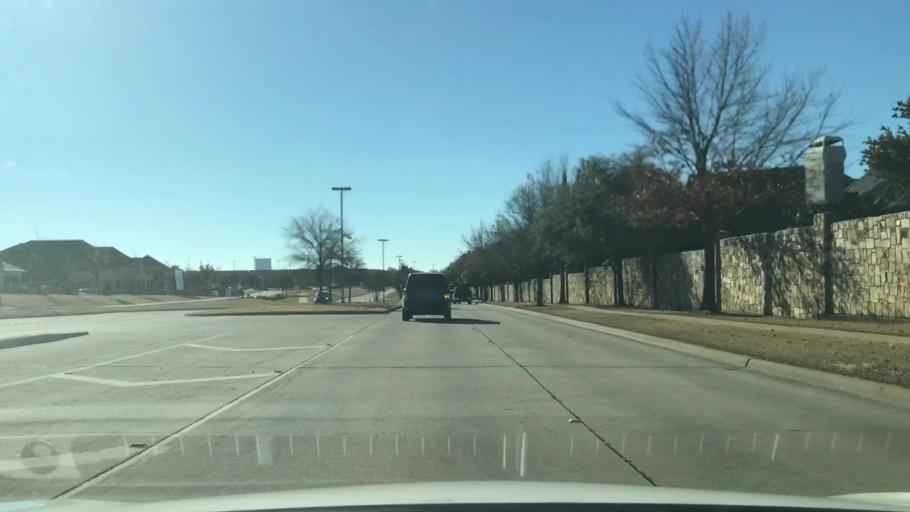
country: US
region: Texas
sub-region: Denton County
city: The Colony
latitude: 33.1055
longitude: -96.8416
